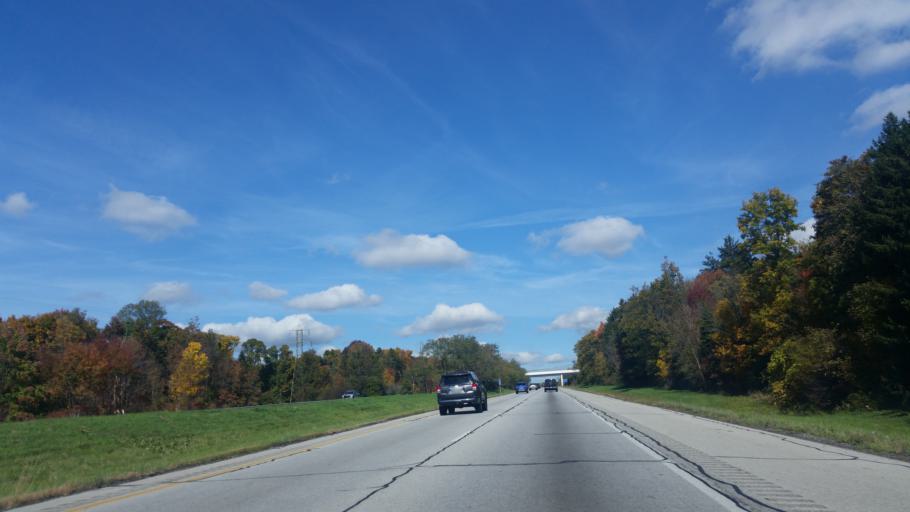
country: US
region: Ohio
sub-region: Summit County
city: Montrose-Ghent
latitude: 41.1715
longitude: -81.6258
